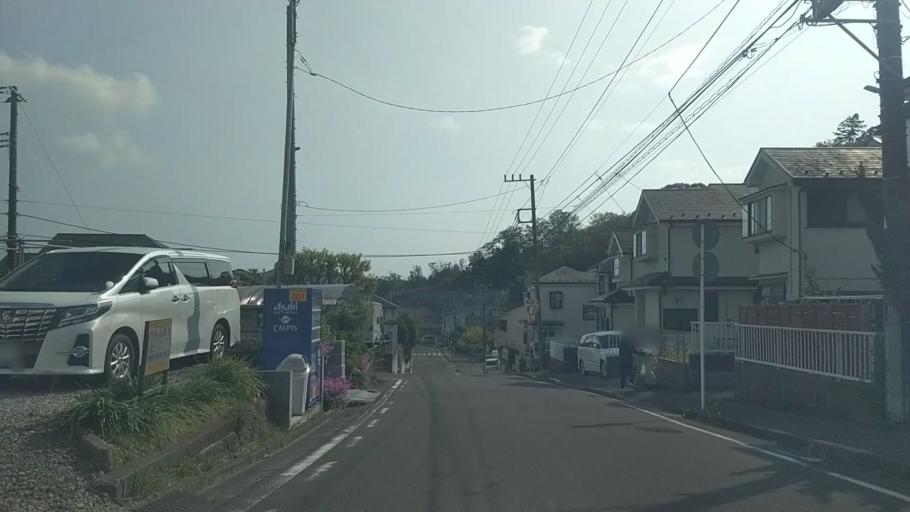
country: JP
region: Kanagawa
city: Kamakura
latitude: 35.3765
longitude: 139.5555
